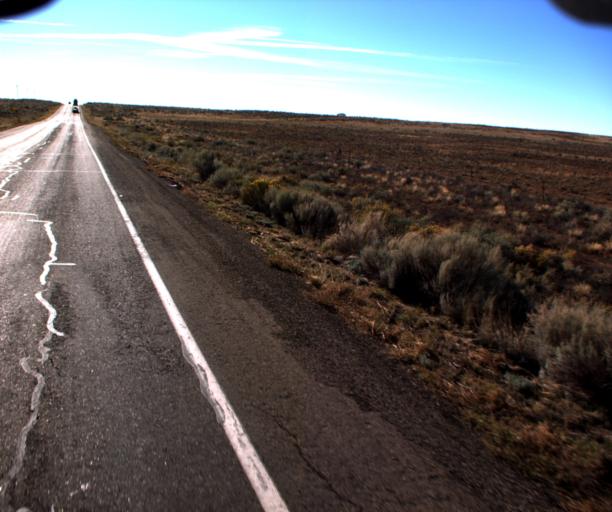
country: US
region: Arizona
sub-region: Mohave County
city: Colorado City
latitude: 36.9195
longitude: -112.9346
